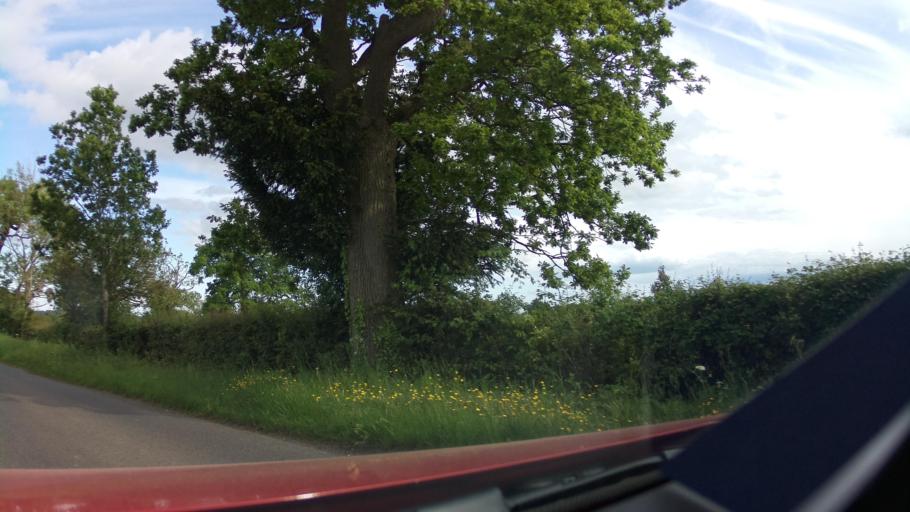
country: GB
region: England
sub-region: Gloucestershire
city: Moreton in Marsh
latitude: 51.9996
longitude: -1.7154
